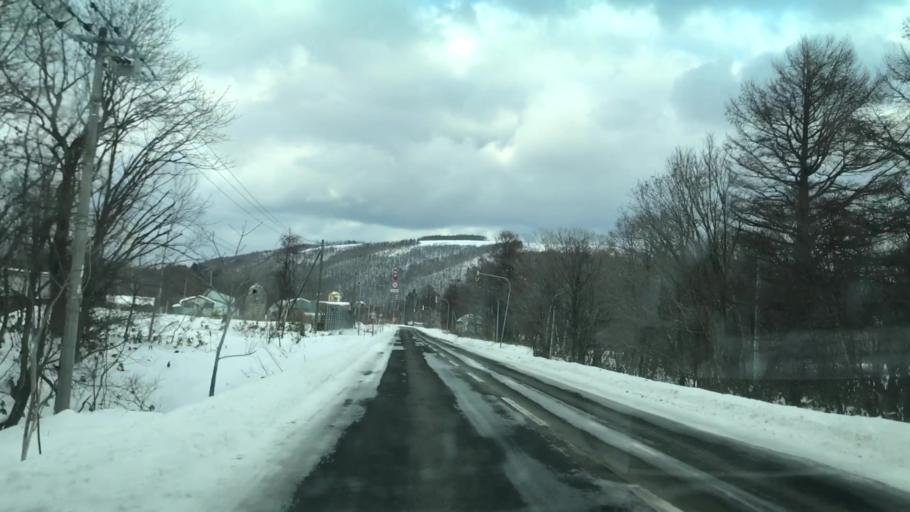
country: JP
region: Hokkaido
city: Yoichi
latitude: 43.3138
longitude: 140.5436
